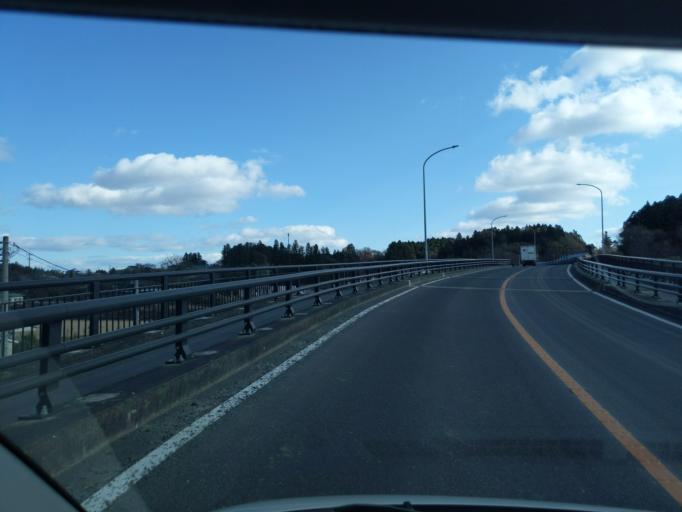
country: JP
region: Miyagi
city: Wakuya
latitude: 38.7081
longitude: 141.1126
